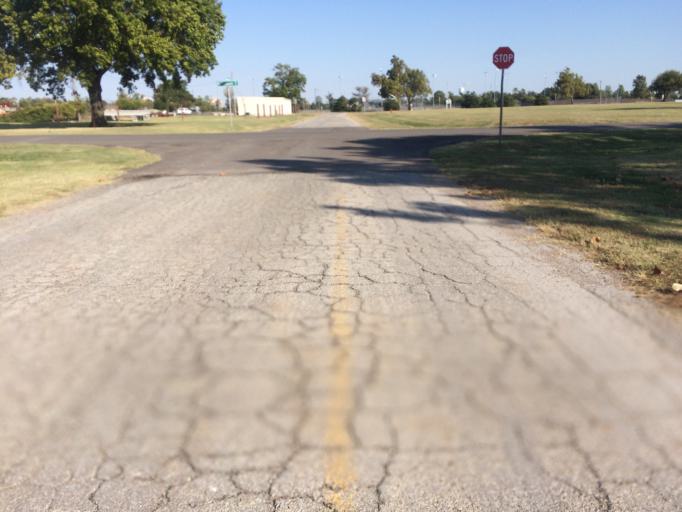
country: US
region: Oklahoma
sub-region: Cleveland County
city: Norman
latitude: 35.1890
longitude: -97.4369
